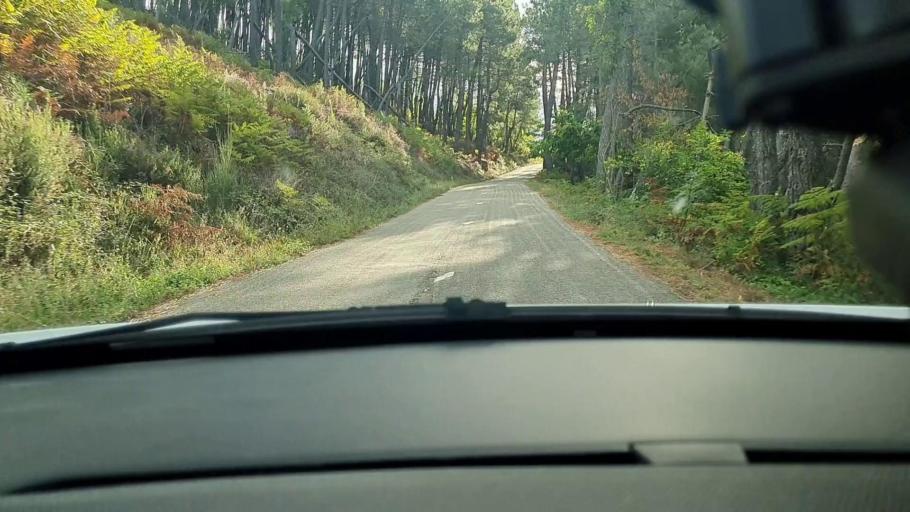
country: FR
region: Languedoc-Roussillon
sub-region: Departement du Gard
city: Besseges
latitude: 44.3501
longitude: 4.0036
